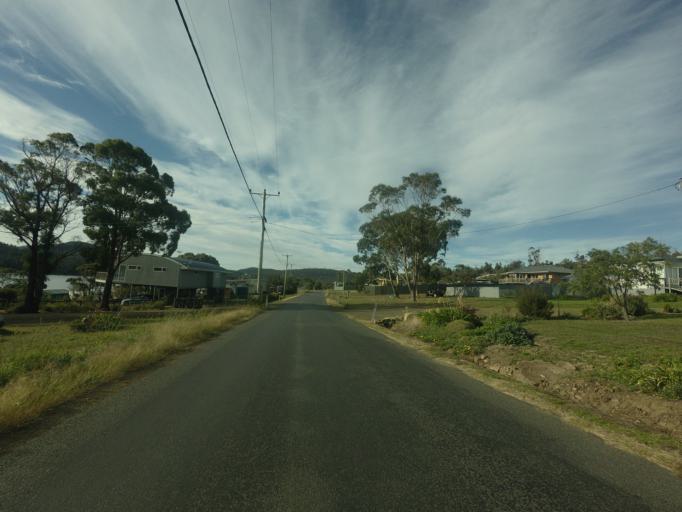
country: AU
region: Tasmania
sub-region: Sorell
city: Sorell
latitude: -42.9485
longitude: 147.8518
